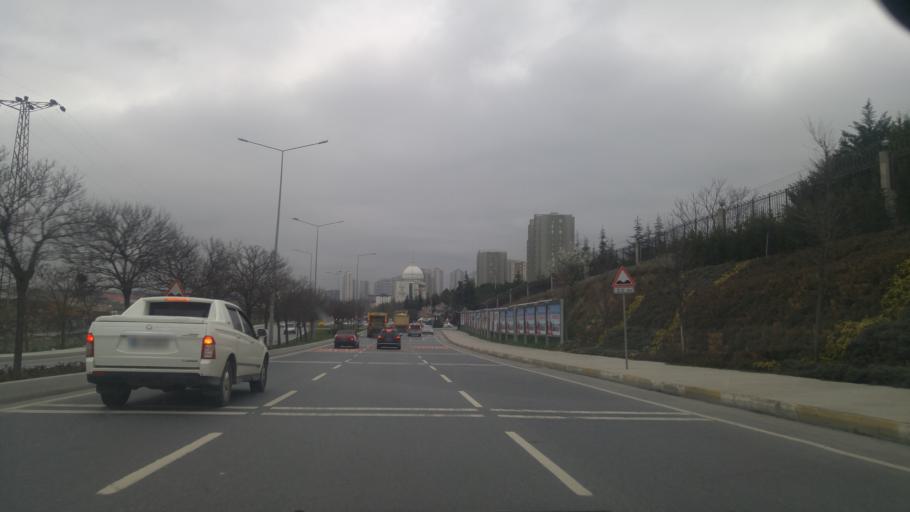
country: TR
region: Istanbul
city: Mahmutbey
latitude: 41.0454
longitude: 28.7741
